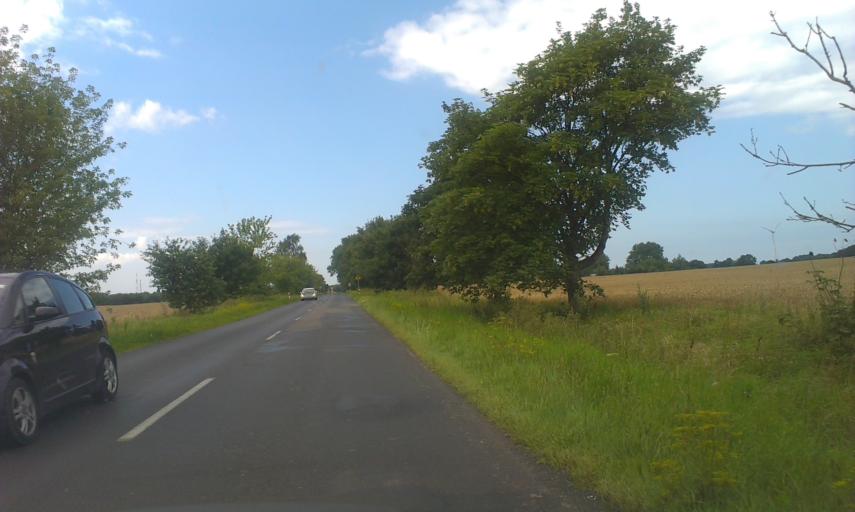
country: PL
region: West Pomeranian Voivodeship
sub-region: Powiat kolobrzeski
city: Dygowo
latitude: 54.1449
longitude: 15.6829
